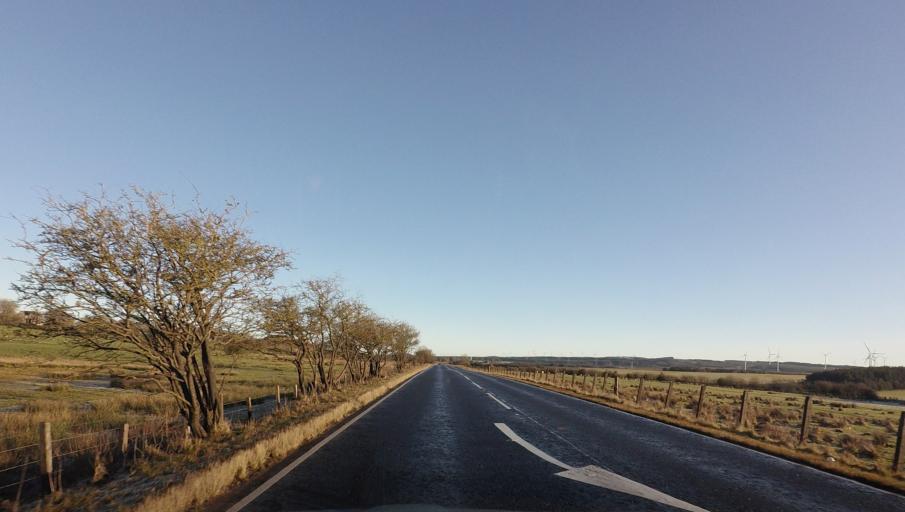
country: GB
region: Scotland
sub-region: North Lanarkshire
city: Shotts
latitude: 55.8055
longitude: -3.7633
